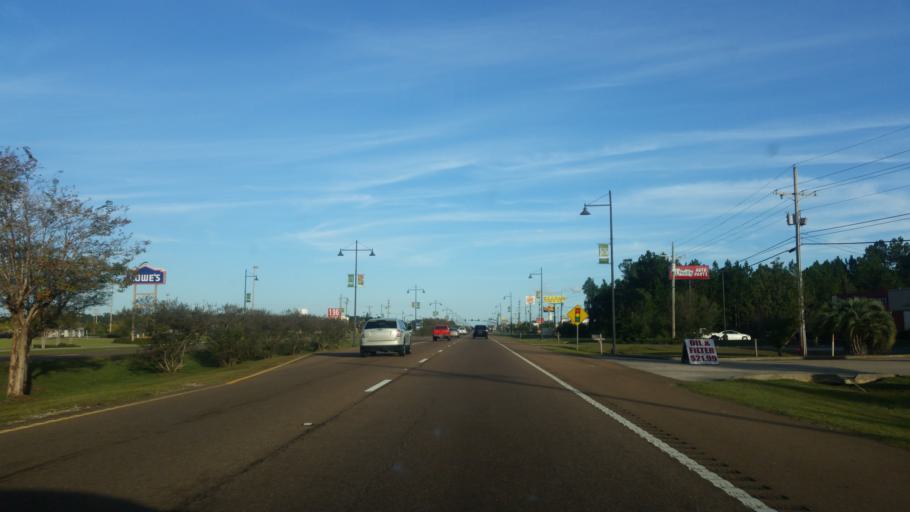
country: US
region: Mississippi
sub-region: Jackson County
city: Gautier
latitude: 30.3936
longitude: -88.6632
